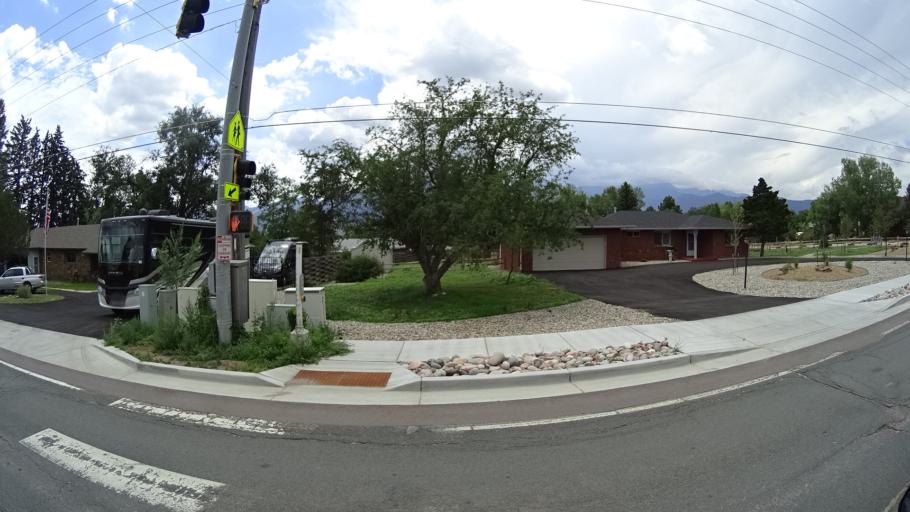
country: US
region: Colorado
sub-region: El Paso County
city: Colorado Springs
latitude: 38.8675
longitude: -104.8575
